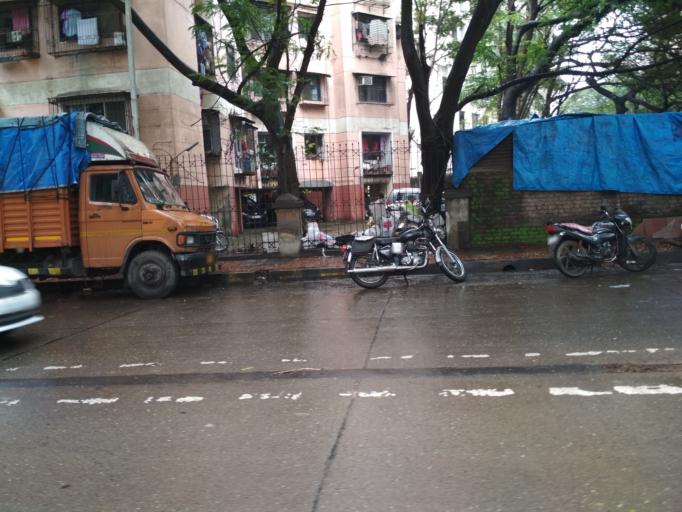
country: IN
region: Maharashtra
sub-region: Thane
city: Thane
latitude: 19.1640
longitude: 72.9422
